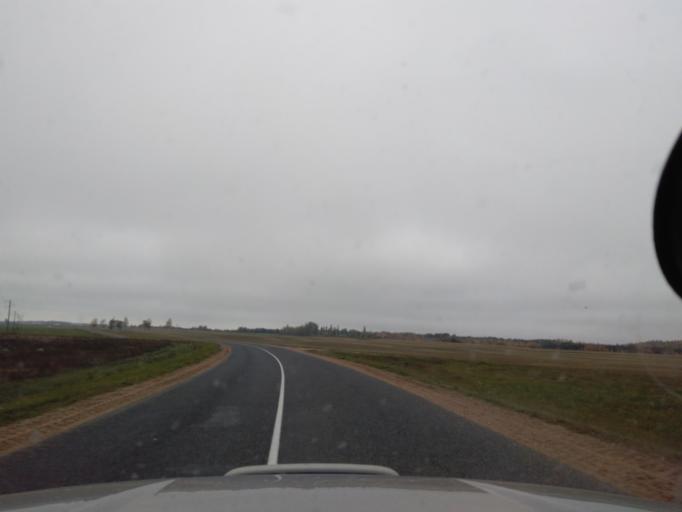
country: BY
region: Minsk
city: Kapyl'
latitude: 53.1541
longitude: 27.1813
